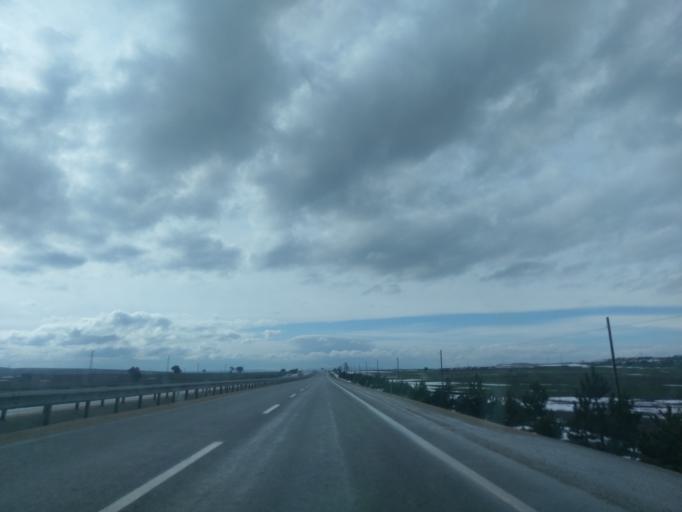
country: TR
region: Eskisehir
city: Inonu
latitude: 39.7236
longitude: 30.2653
